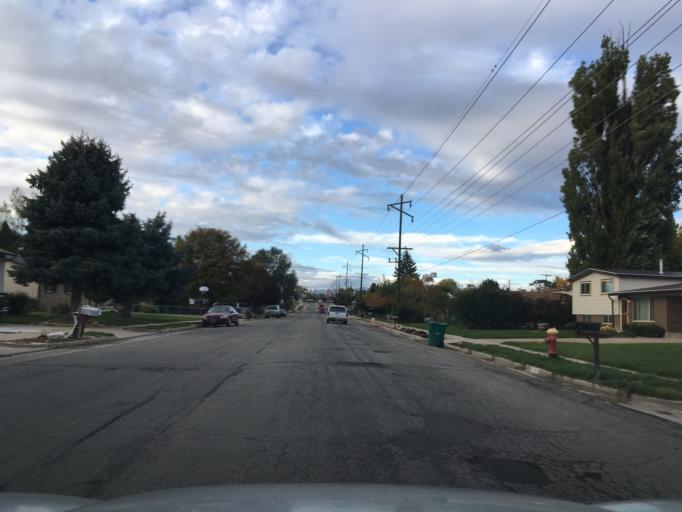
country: US
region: Utah
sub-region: Davis County
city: Layton
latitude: 41.0763
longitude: -111.9879
